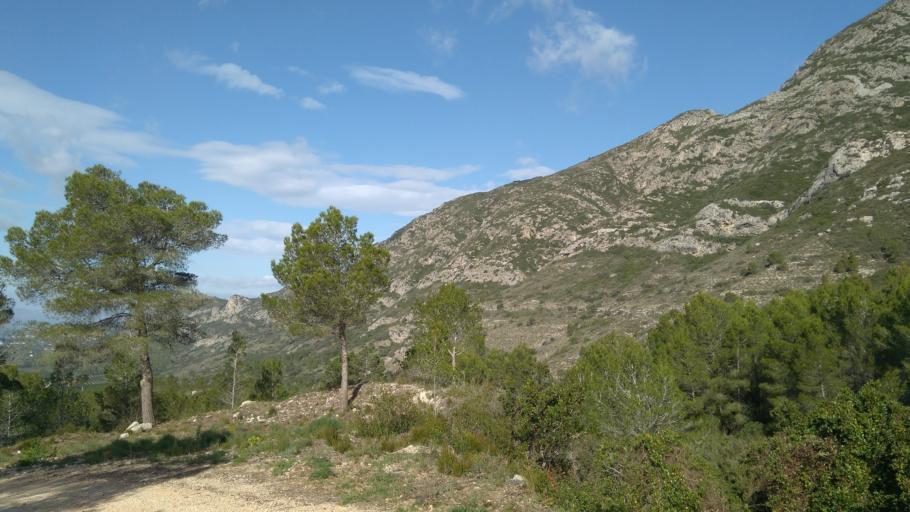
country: ES
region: Valencia
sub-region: Provincia de Valencia
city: Llauri
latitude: 39.1115
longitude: -0.3400
